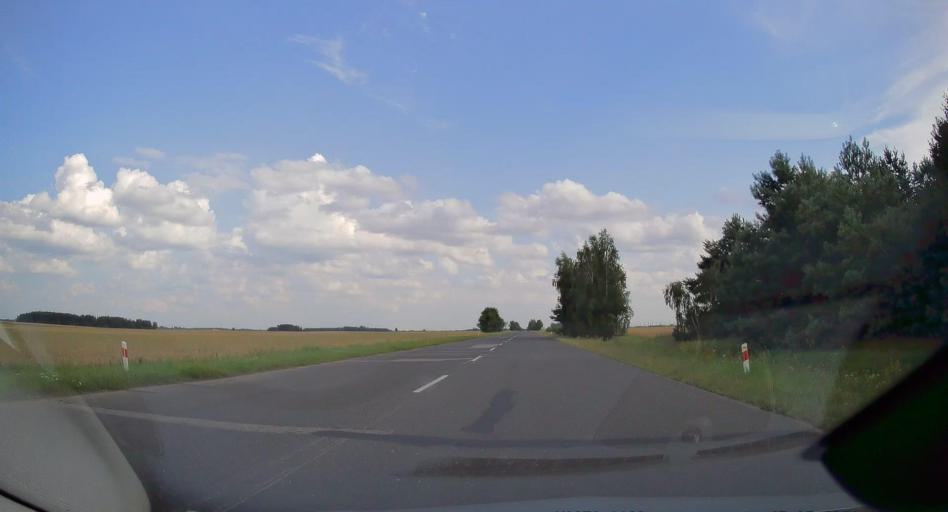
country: PL
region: Lodz Voivodeship
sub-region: Powiat tomaszowski
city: Rzeczyca
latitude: 51.6604
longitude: 20.2704
